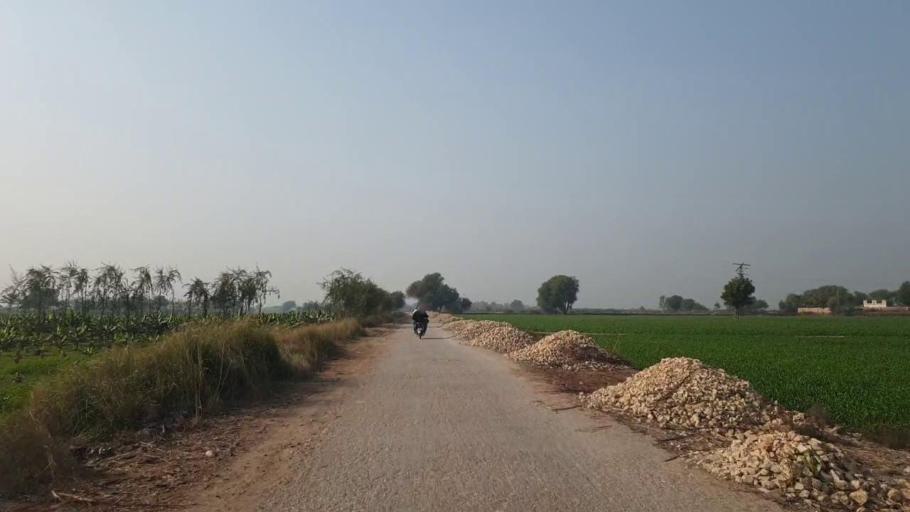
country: PK
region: Sindh
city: Shahdadpur
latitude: 25.9678
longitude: 68.5536
